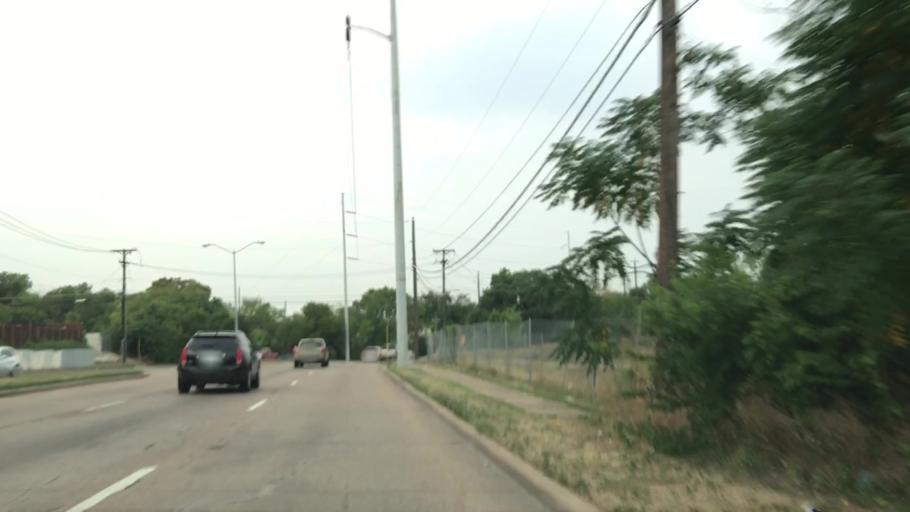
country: US
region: Texas
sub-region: Dallas County
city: Cockrell Hill
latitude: 32.7610
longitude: -96.8728
